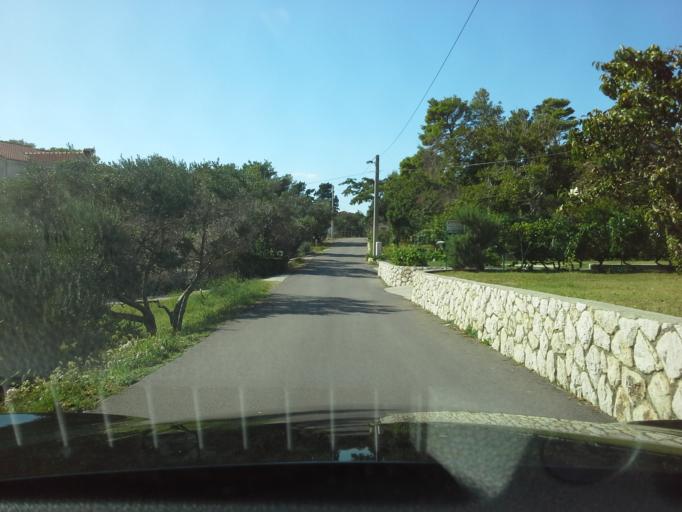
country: HR
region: Primorsko-Goranska
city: Banjol
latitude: 44.7466
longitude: 14.7880
